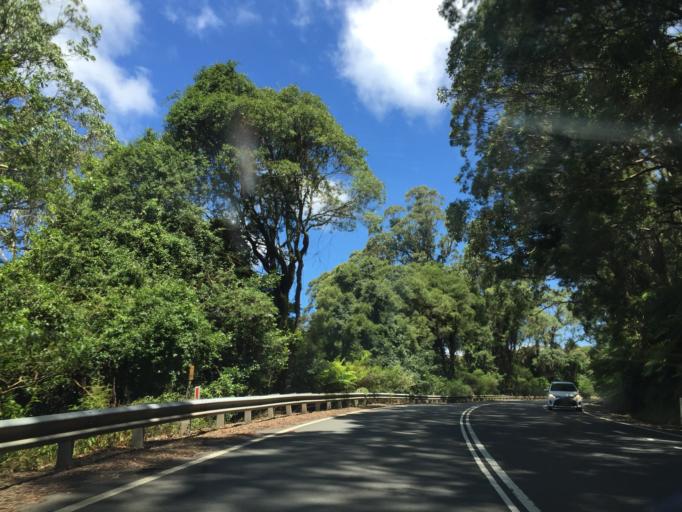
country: AU
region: New South Wales
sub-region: Blue Mountains Municipality
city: Blackheath
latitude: -33.5446
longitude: 150.4259
